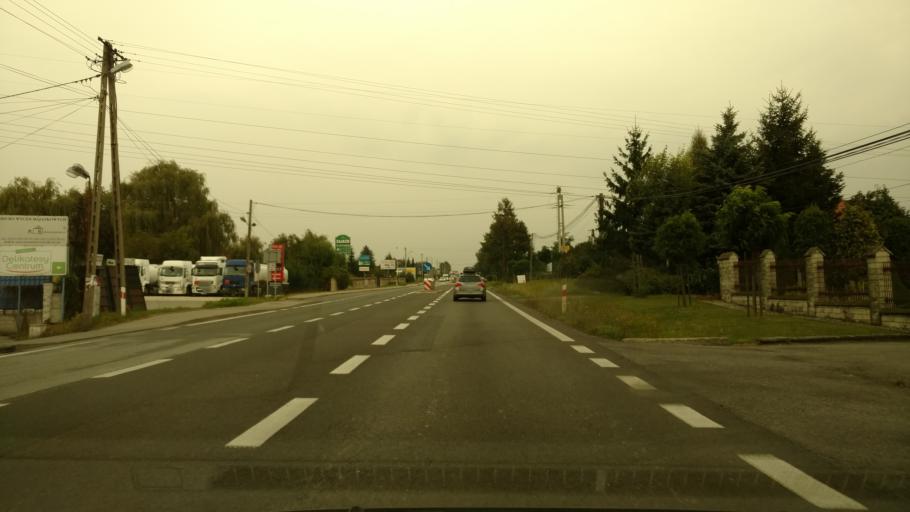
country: PL
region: Lesser Poland Voivodeship
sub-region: Powiat krakowski
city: Michalowice
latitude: 50.1233
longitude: 19.9677
